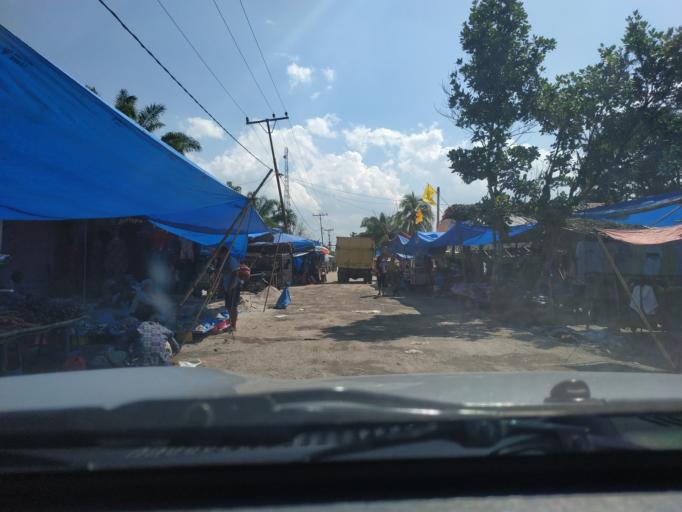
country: ID
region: North Sumatra
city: Tanjungbalai
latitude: 2.8757
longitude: 99.8607
